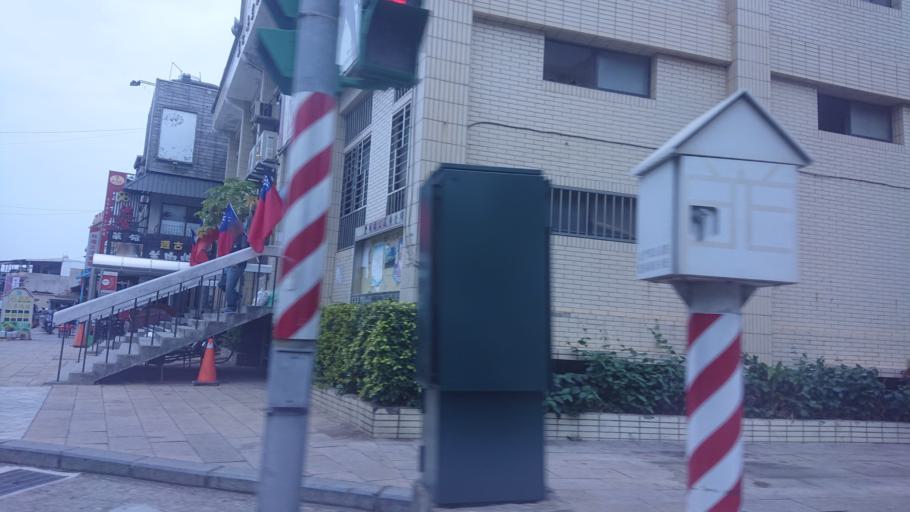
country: TW
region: Fukien
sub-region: Kinmen
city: Jincheng
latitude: 24.4334
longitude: 118.3146
